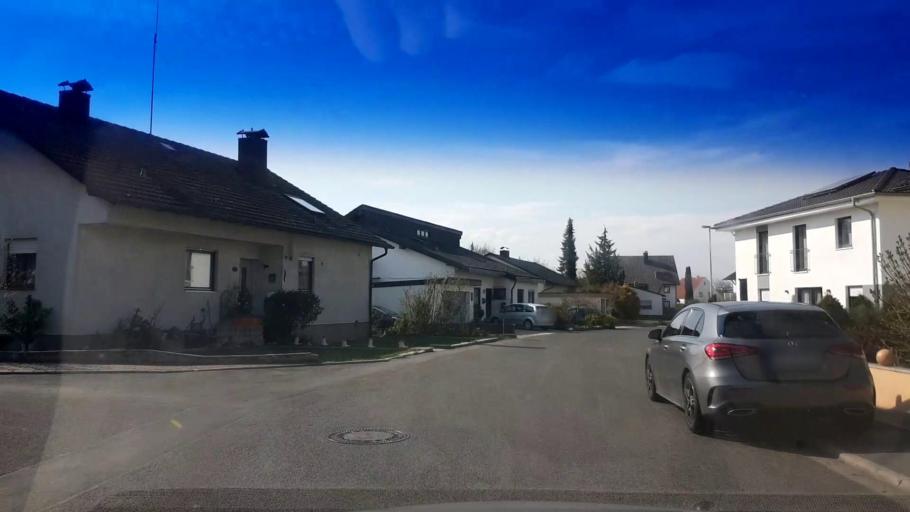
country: DE
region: Bavaria
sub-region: Upper Franconia
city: Zapfendorf
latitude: 50.0130
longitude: 10.9319
